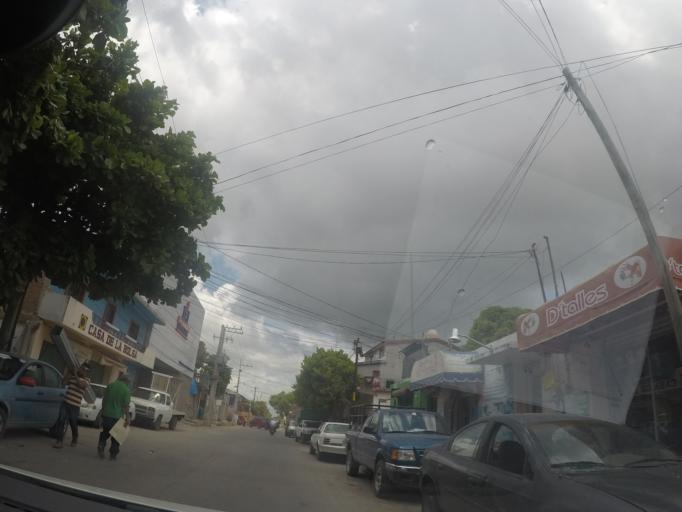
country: MX
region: Oaxaca
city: Juchitan de Zaragoza
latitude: 16.4333
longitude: -95.0238
